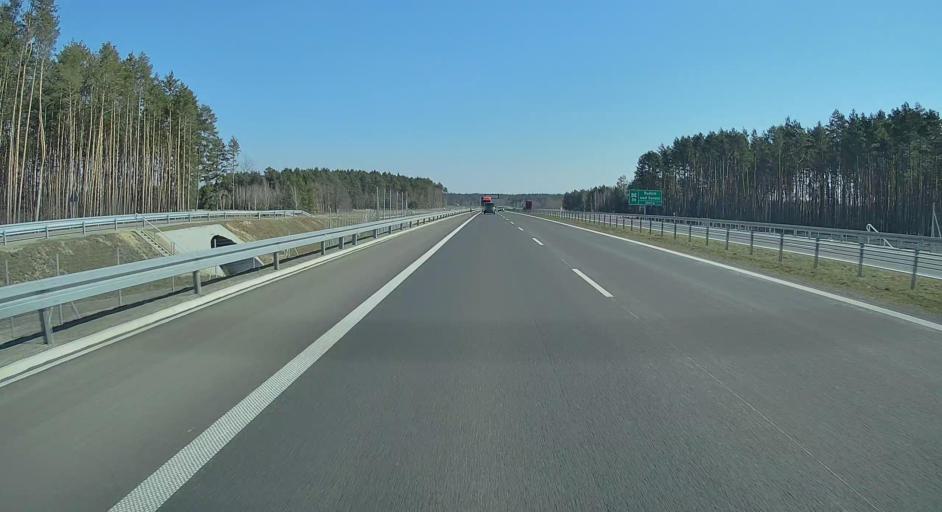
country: PL
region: Subcarpathian Voivodeship
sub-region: Powiat nizanski
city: Raclawice
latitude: 50.4738
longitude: 22.1638
